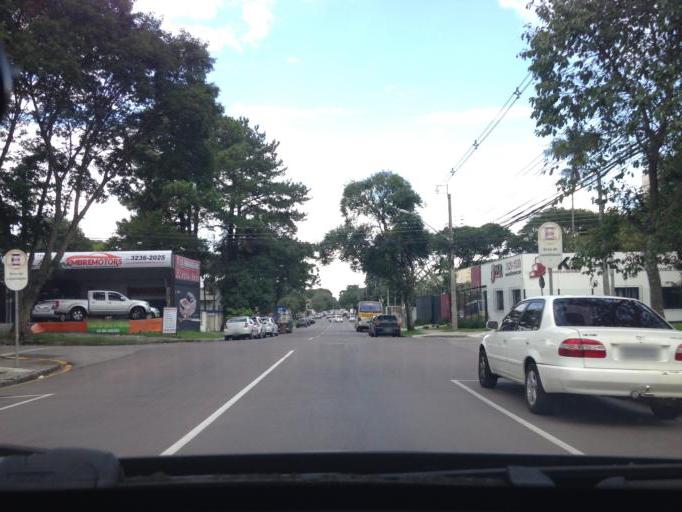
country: BR
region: Parana
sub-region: Curitiba
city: Curitiba
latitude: -25.4063
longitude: -49.2414
